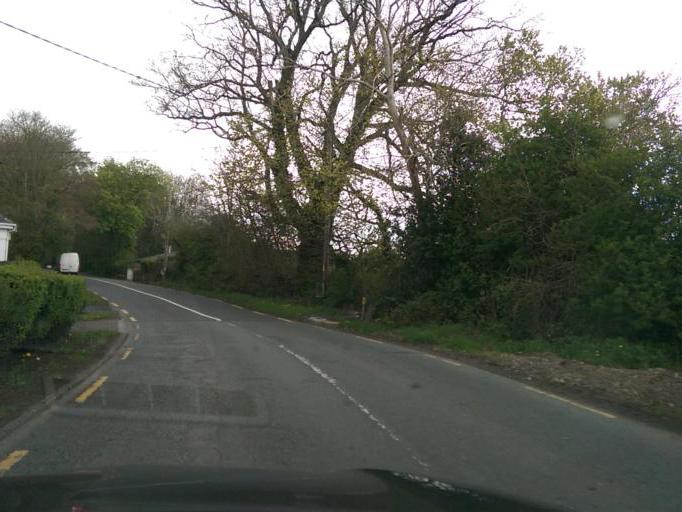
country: IE
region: Leinster
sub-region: An Mhi
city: Dunboyne
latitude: 53.3934
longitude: -6.4488
